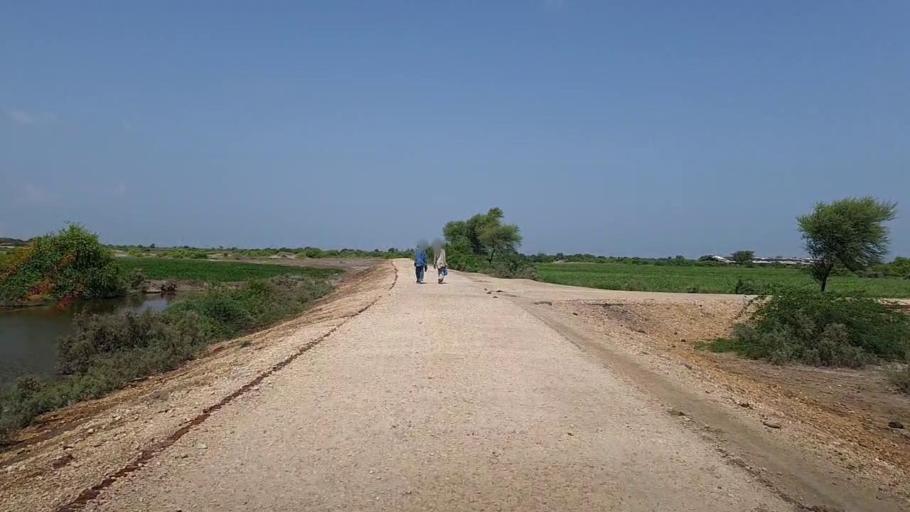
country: PK
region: Sindh
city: Mirpur Batoro
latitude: 24.6495
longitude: 68.4258
